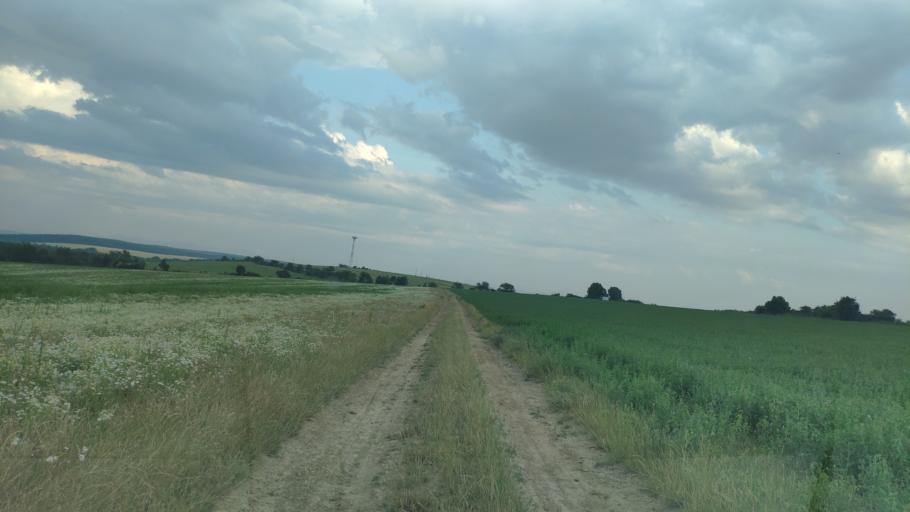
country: SK
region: Kosicky
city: Moldava nad Bodvou
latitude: 48.6895
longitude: 20.9901
